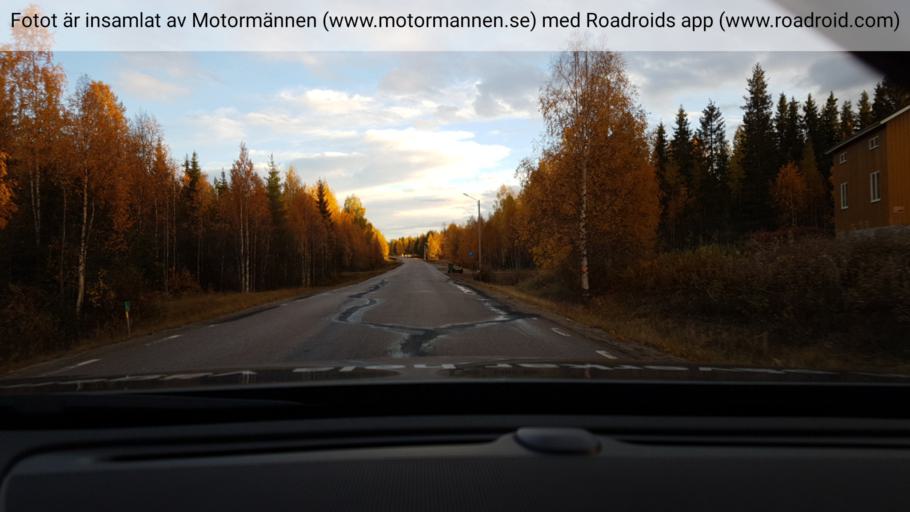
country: SE
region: Norrbotten
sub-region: Overkalix Kommun
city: OEverkalix
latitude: 66.6294
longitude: 22.7337
